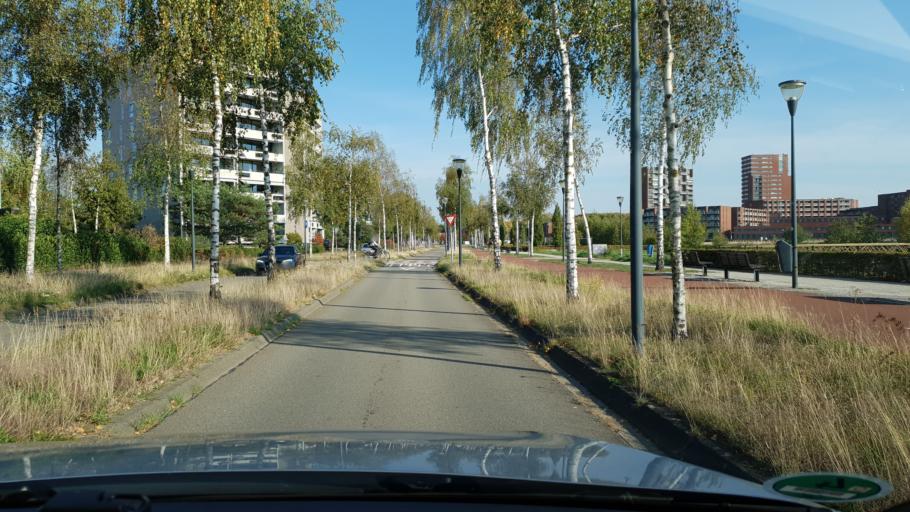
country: NL
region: North Brabant
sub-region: Gemeente Eindhoven
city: Meerhoven
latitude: 51.4450
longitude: 5.4032
